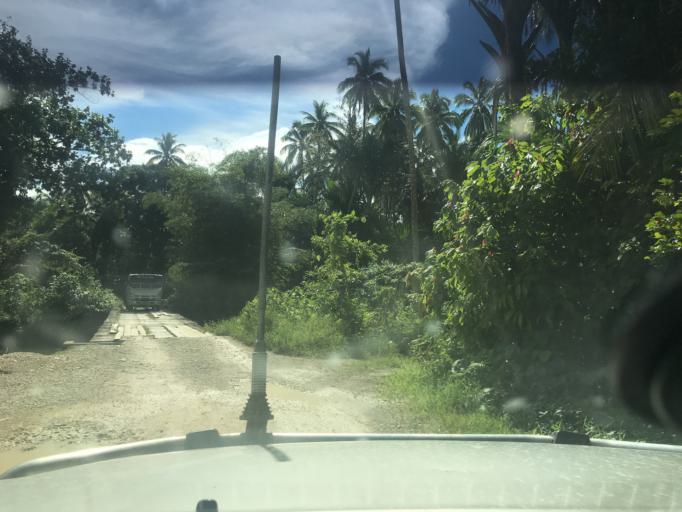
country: SB
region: Malaita
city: Auki
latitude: -8.3687
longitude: 160.6719
